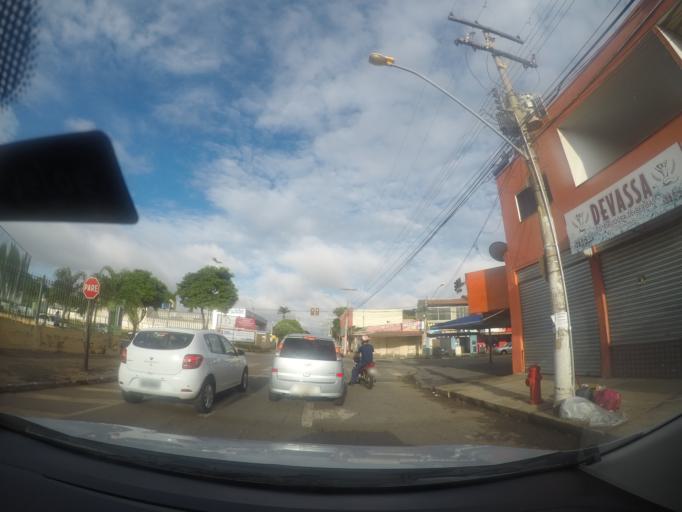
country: BR
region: Goias
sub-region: Goiania
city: Goiania
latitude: -16.6902
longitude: -49.3108
